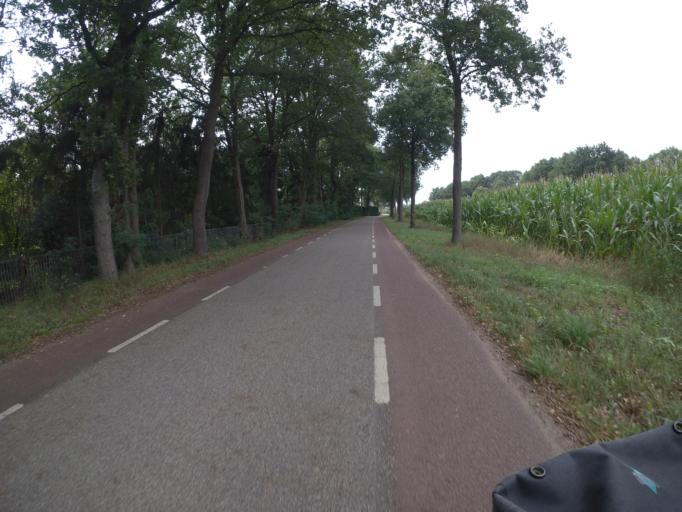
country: NL
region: North Brabant
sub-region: Gemeente Maasdonk
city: Geffen
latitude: 51.7355
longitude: 5.4806
